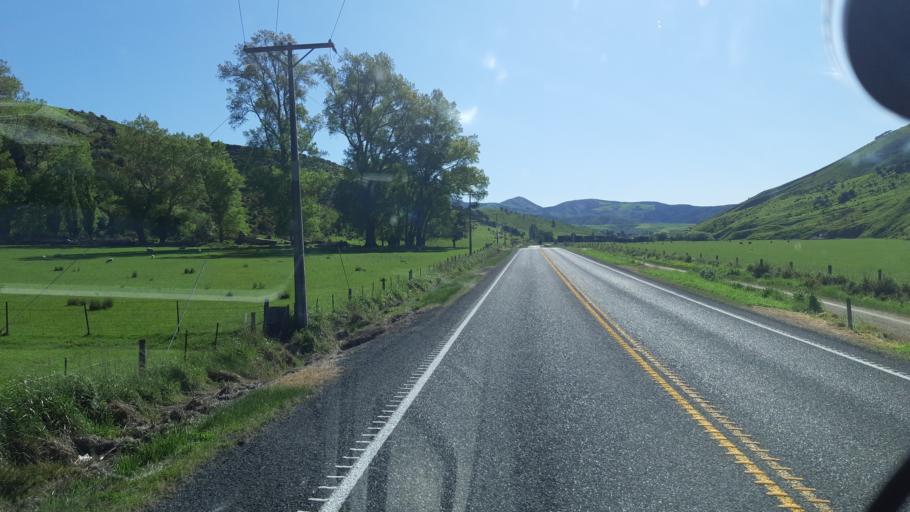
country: NZ
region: Otago
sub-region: Clutha District
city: Balclutha
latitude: -45.8296
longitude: 169.5579
